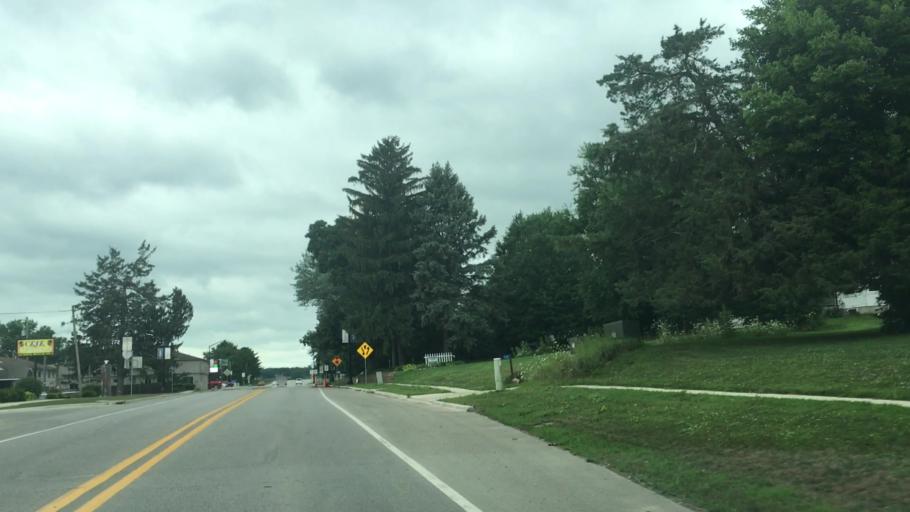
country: US
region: Iowa
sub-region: Johnson County
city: Tiffin
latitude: 41.7071
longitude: -91.6635
